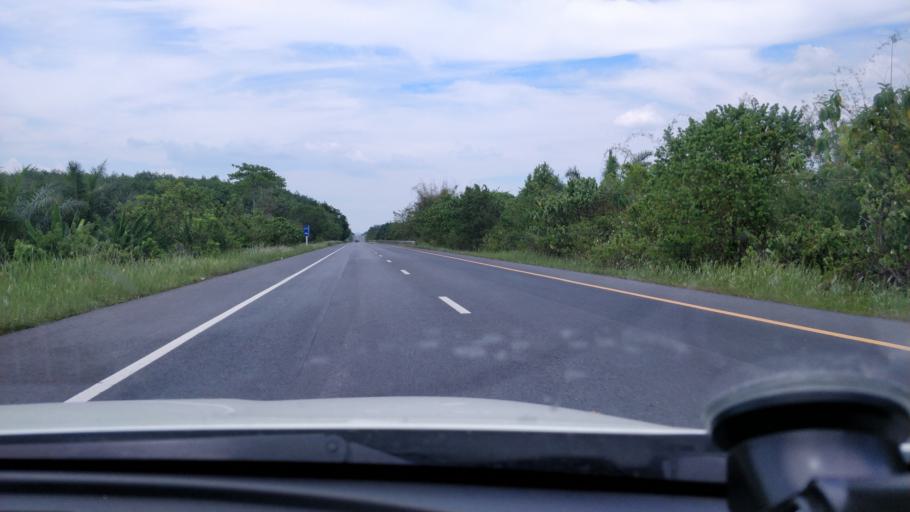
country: TH
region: Krabi
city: Plai Phraya
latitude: 8.4620
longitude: 98.8619
